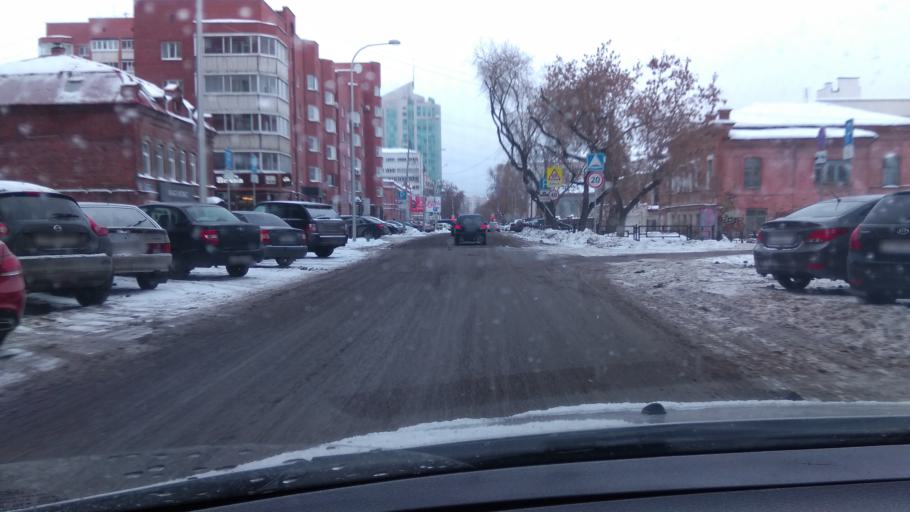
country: RU
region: Sverdlovsk
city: Yekaterinburg
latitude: 56.8311
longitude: 60.5933
